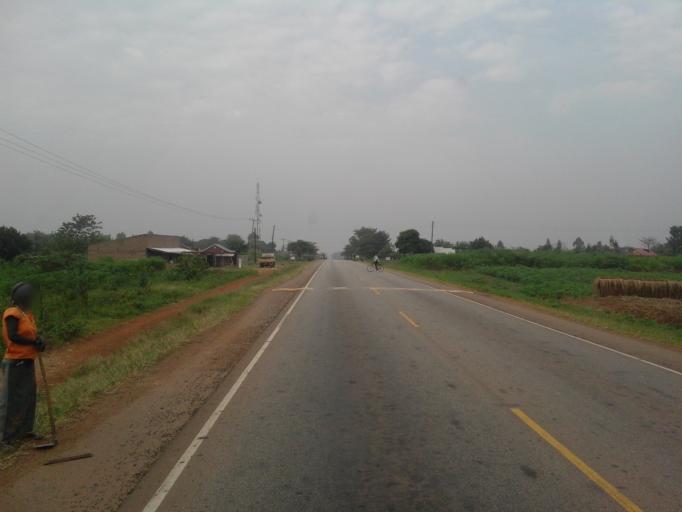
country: UG
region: Eastern Region
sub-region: Tororo District
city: Tororo
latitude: 0.6263
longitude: 34.1000
